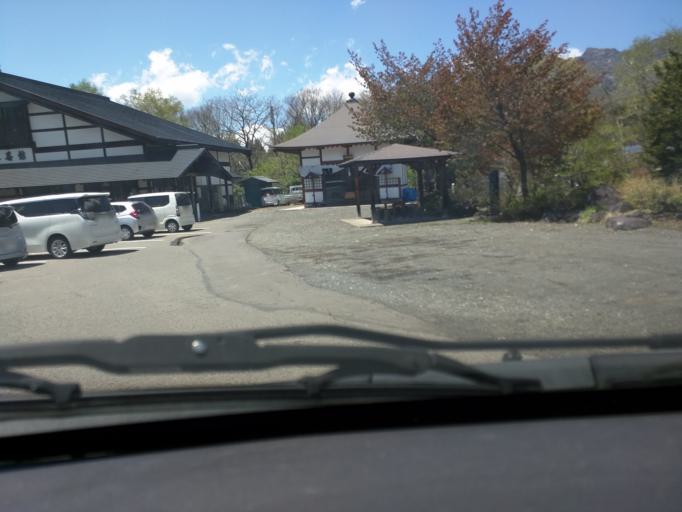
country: JP
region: Nagano
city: Nagano-shi
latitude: 36.7276
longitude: 138.0775
